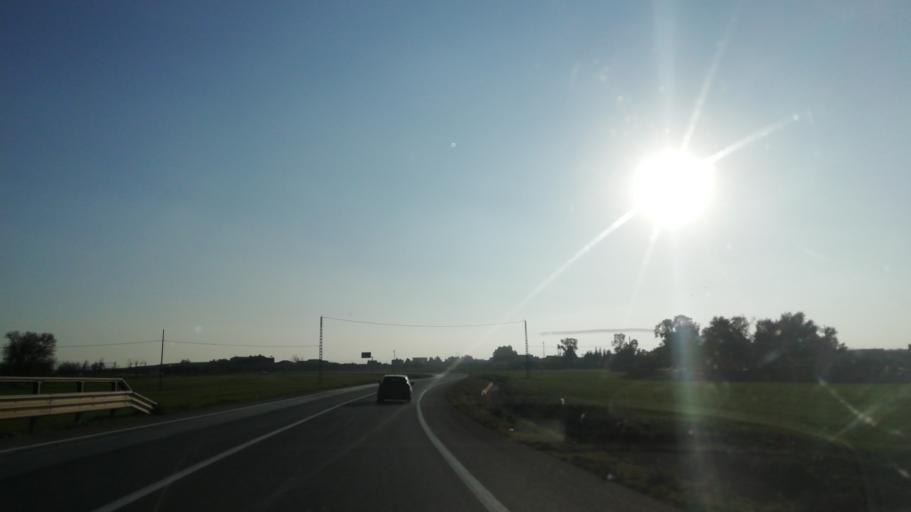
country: DZ
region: Sidi Bel Abbes
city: Sidi Bel Abbes
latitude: 35.1717
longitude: -0.6862
